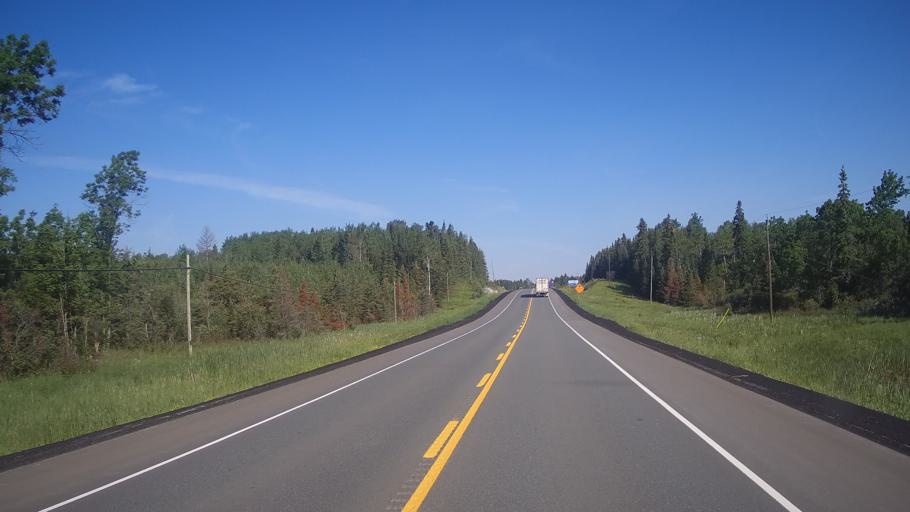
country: CA
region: Ontario
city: Dryden
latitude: 49.6657
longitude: -92.4869
